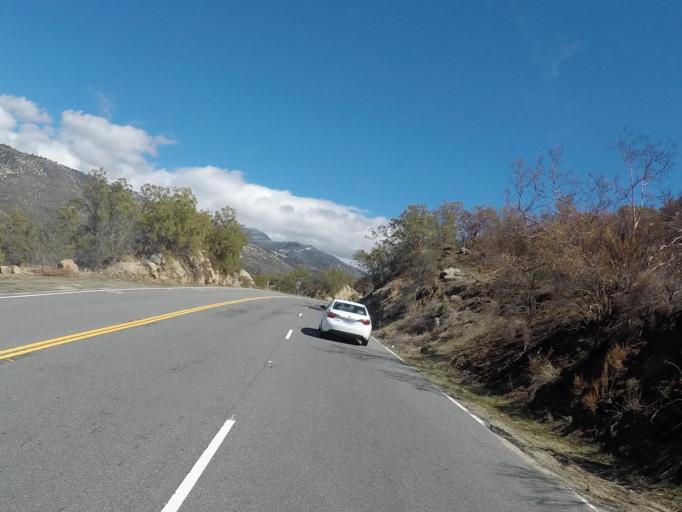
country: US
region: California
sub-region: Riverside County
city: Idyllwild-Pine Cove
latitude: 33.7014
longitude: -116.7703
